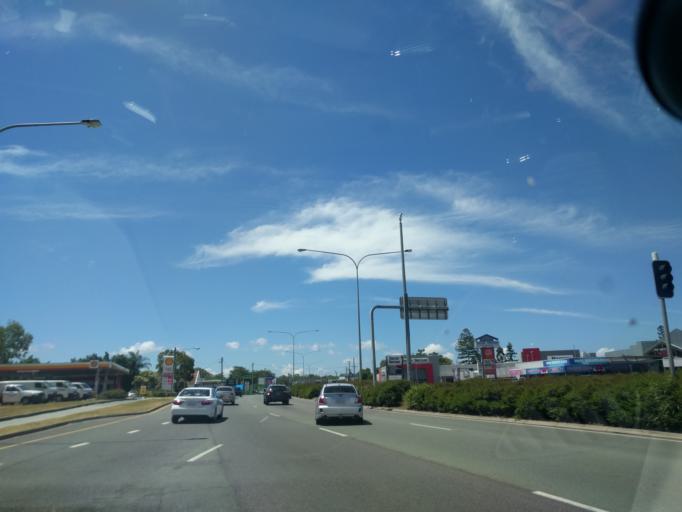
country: AU
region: Queensland
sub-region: Brisbane
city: Bridegman Downs
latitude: -27.3606
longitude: 153.0168
